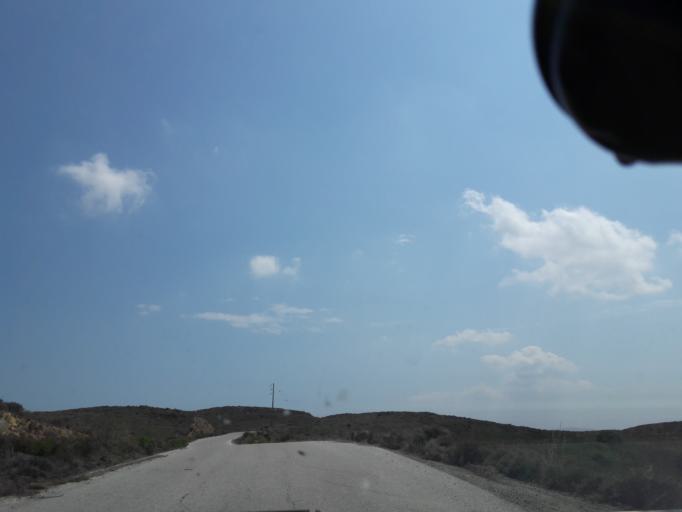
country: GR
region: North Aegean
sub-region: Nomos Lesvou
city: Myrina
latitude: 39.9773
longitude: 25.3504
